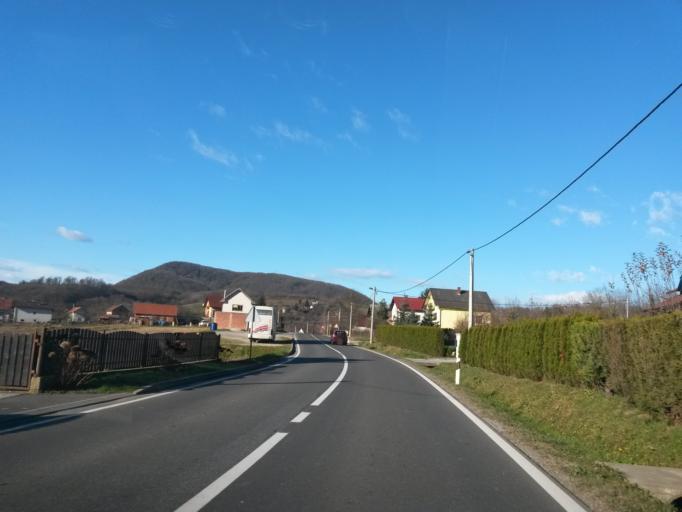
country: HR
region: Varazdinska
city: Lepoglava
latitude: 46.2133
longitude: 16.0126
